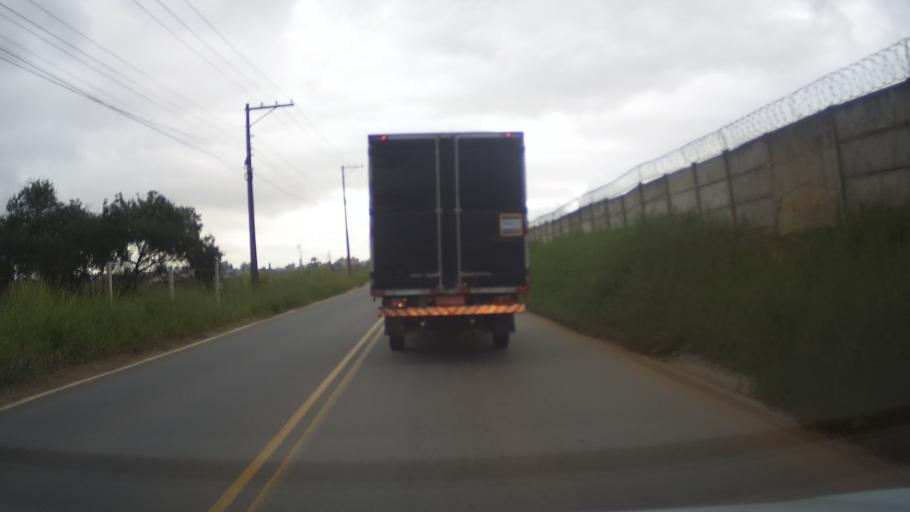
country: BR
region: Sao Paulo
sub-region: Aruja
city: Aruja
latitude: -23.3929
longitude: -46.4096
